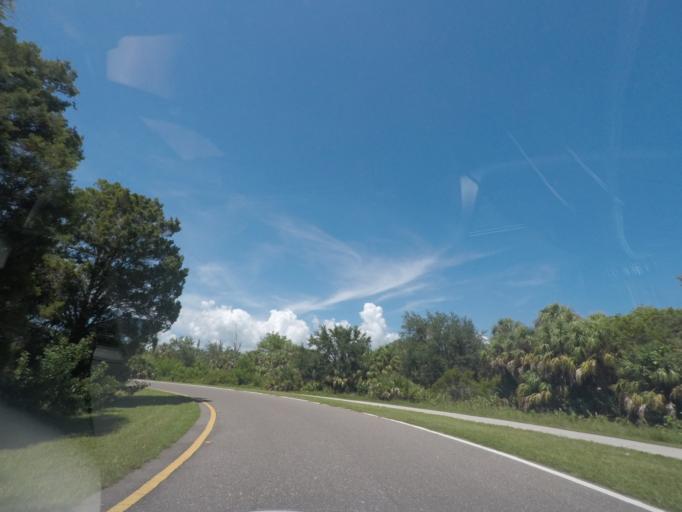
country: US
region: Florida
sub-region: Pinellas County
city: Tierra Verde
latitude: 27.6428
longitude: -82.7386
